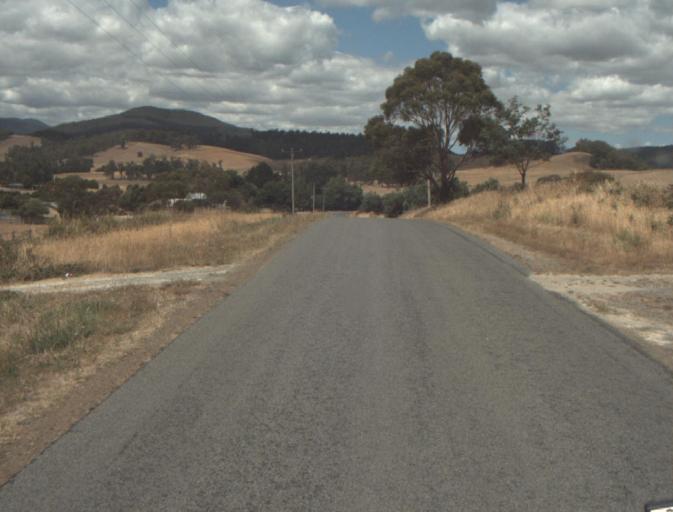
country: AU
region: Tasmania
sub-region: Launceston
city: Mayfield
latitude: -41.2335
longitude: 147.1475
